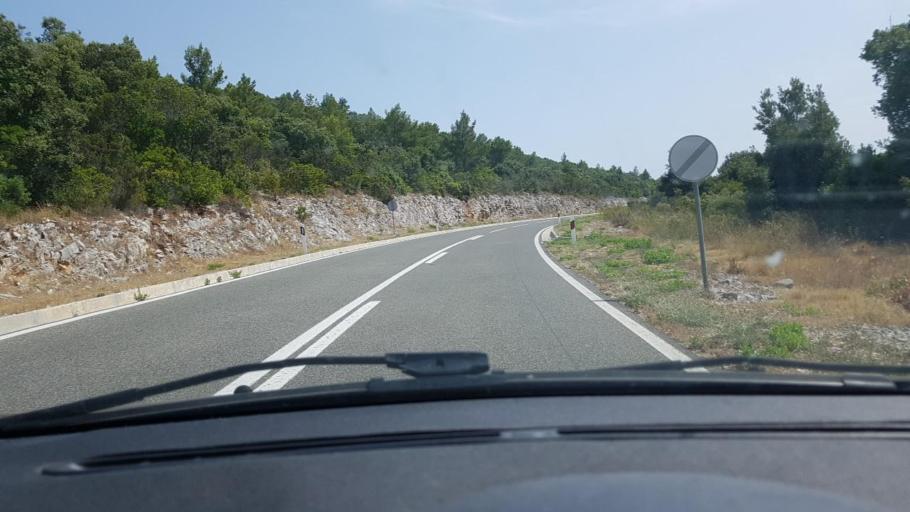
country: HR
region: Dubrovacko-Neretvanska
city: Smokvica
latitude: 42.9545
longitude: 16.9423
